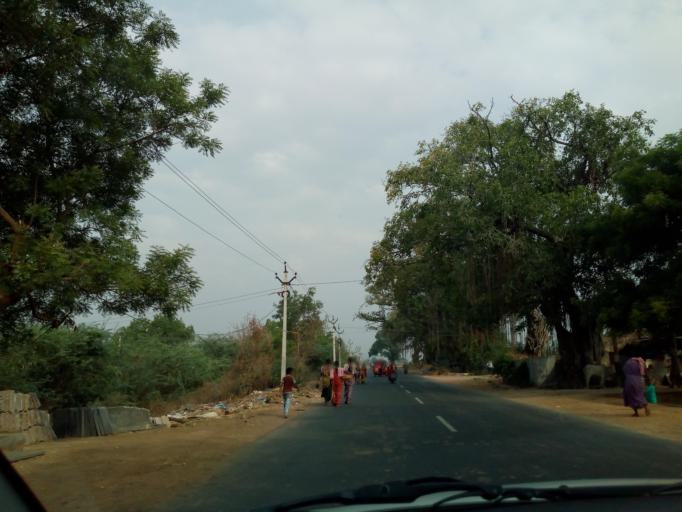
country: IN
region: Andhra Pradesh
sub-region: Prakasam
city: Diguvametta
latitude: 15.3727
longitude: 78.8793
